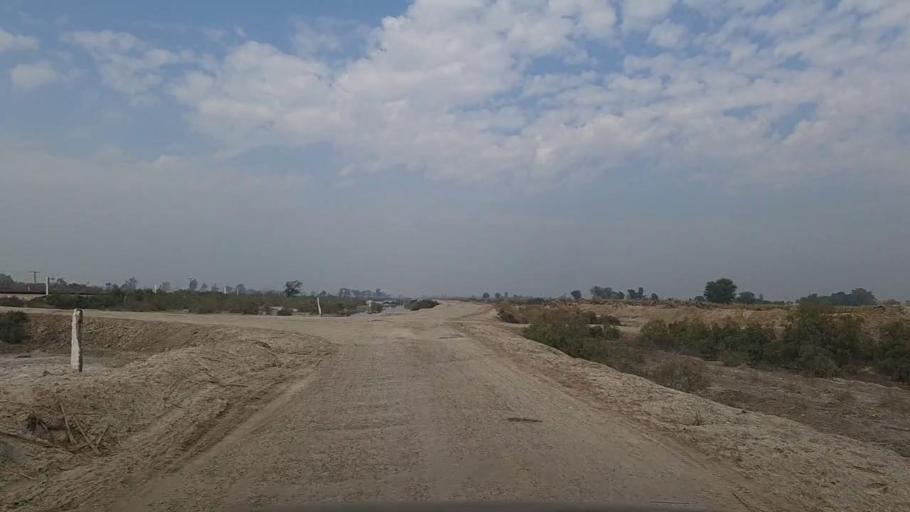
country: PK
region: Sindh
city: Daur
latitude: 26.3690
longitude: 68.3595
